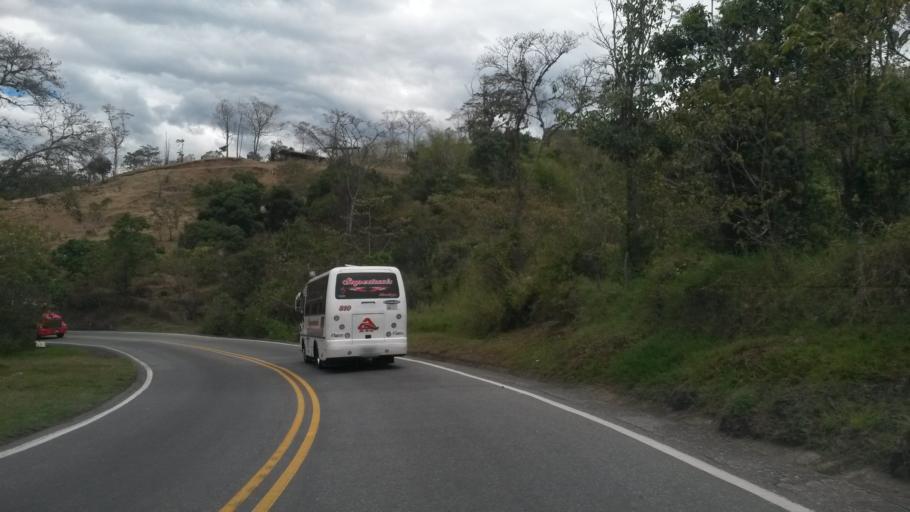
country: CO
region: Cauca
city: Rosas
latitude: 2.2798
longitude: -76.7253
